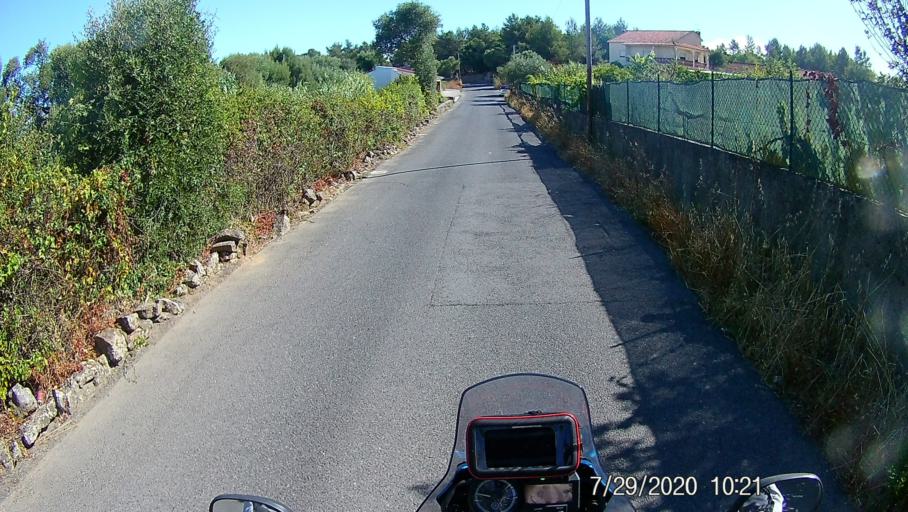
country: PT
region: Lisbon
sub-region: Cascais
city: Estoril
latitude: 38.7264
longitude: -9.3790
